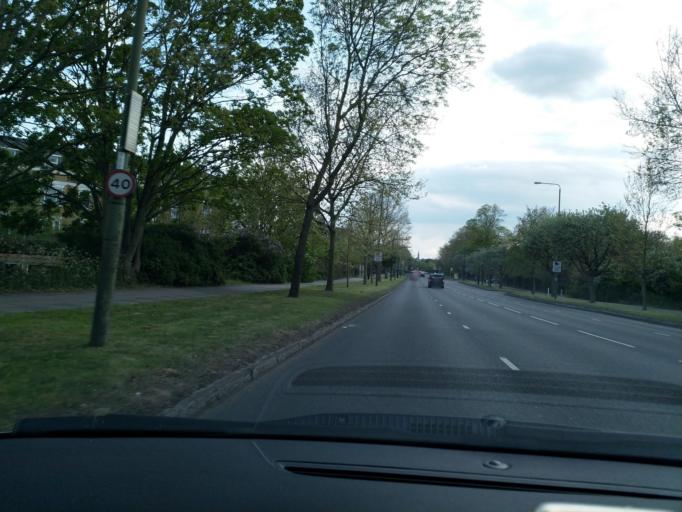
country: GB
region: England
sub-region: Greater London
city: Richmond
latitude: 51.4716
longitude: -0.2720
